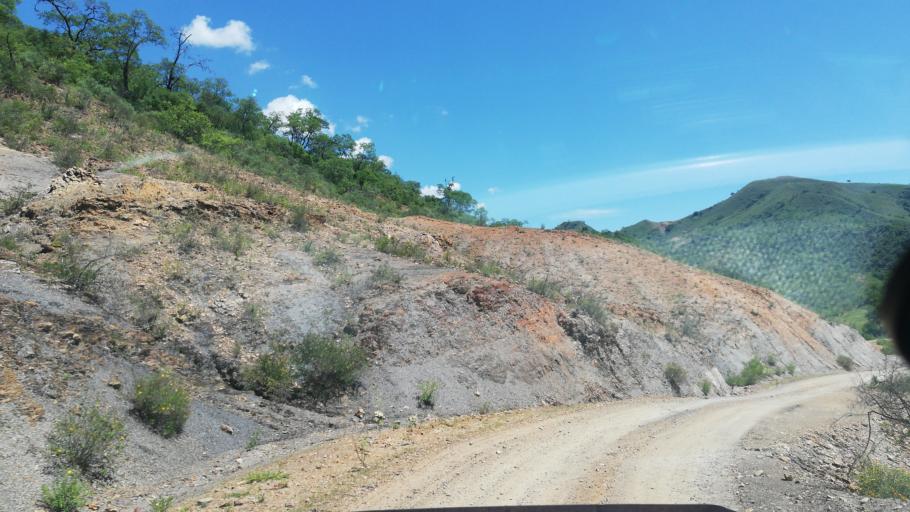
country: BO
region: Cochabamba
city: Mizque
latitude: -17.8422
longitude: -65.3088
